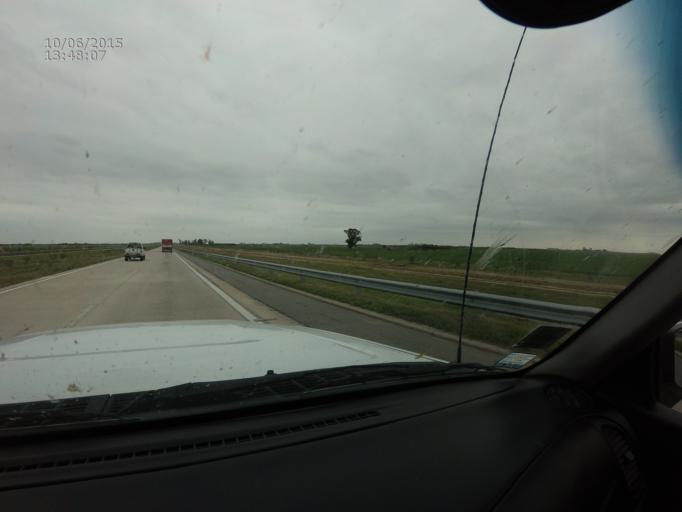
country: AR
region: Cordoba
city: Bell Ville
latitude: -32.5780
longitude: -62.6384
